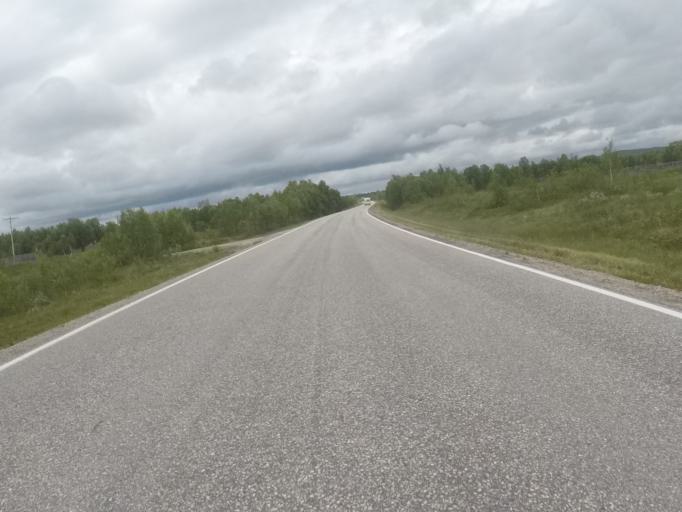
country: FI
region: Lapland
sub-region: Tunturi-Lappi
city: Enontekioe
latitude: 68.4837
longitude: 23.3592
